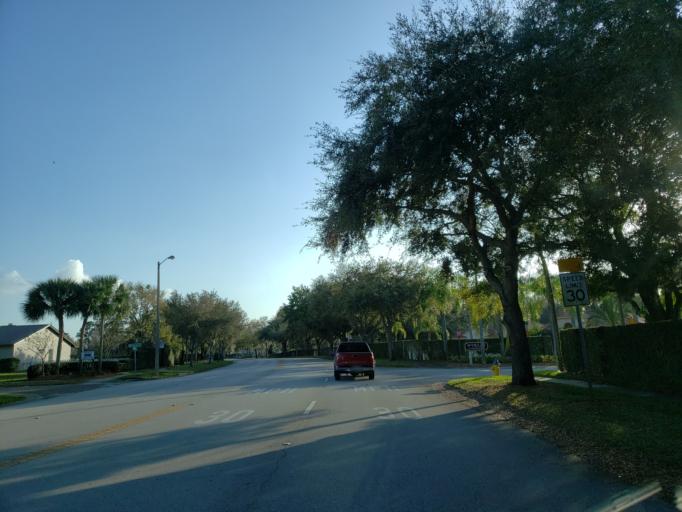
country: US
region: Florida
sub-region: Hillsborough County
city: Bloomingdale
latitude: 27.8838
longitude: -82.2657
